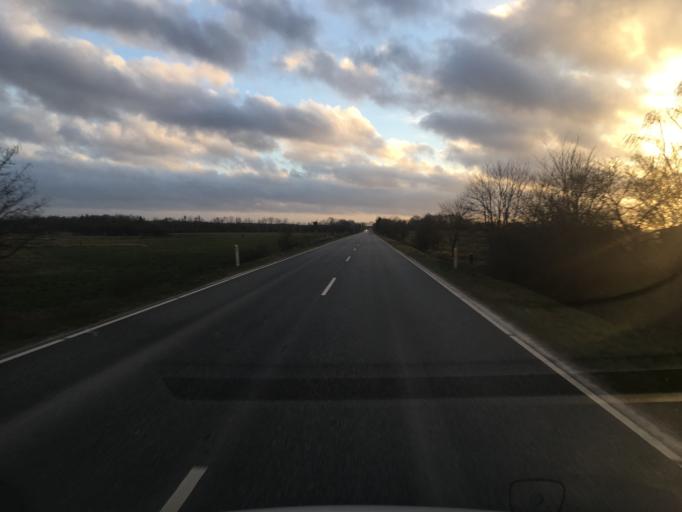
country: DK
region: South Denmark
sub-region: Aabenraa Kommune
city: Tinglev
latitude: 54.9617
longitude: 9.2944
